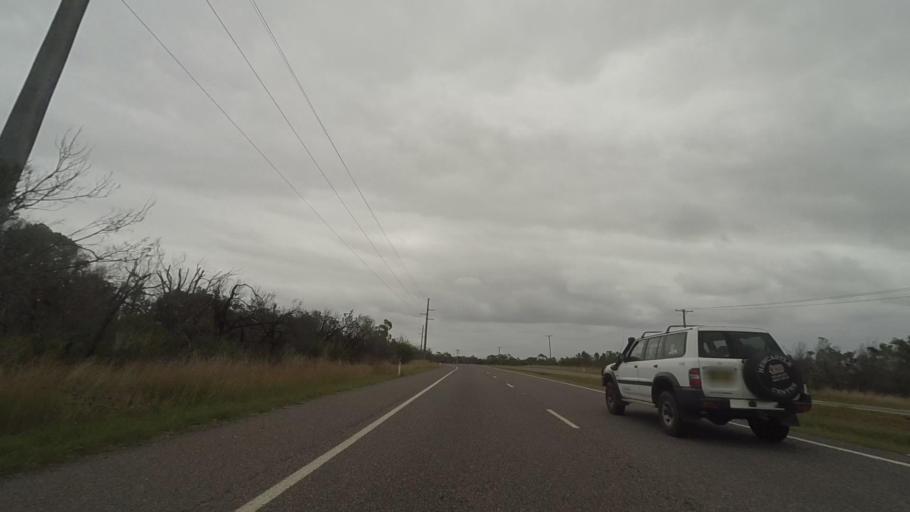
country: AU
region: New South Wales
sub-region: Wyong Shire
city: Kingfisher Shores
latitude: -33.1854
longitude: 151.5877
